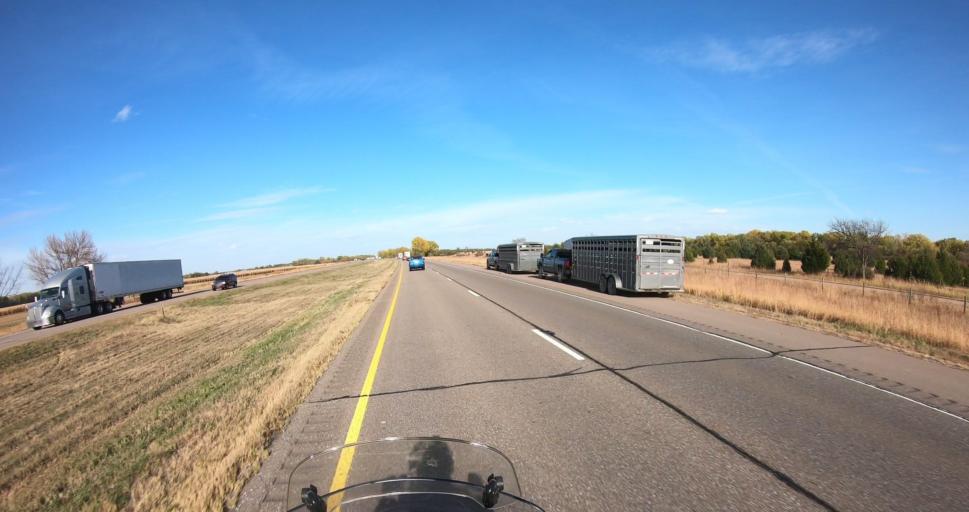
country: US
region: Nebraska
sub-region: Hall County
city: Wood River
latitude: 40.7439
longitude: -98.6238
